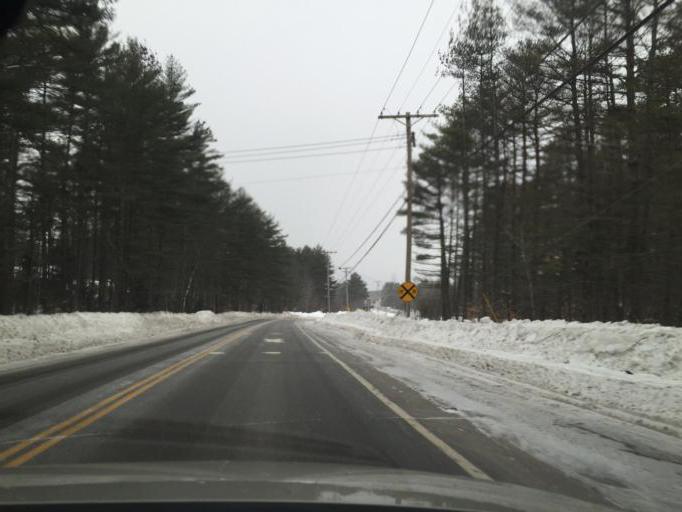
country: US
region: New Hampshire
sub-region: Carroll County
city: North Conway
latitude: 44.0819
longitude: -71.2407
